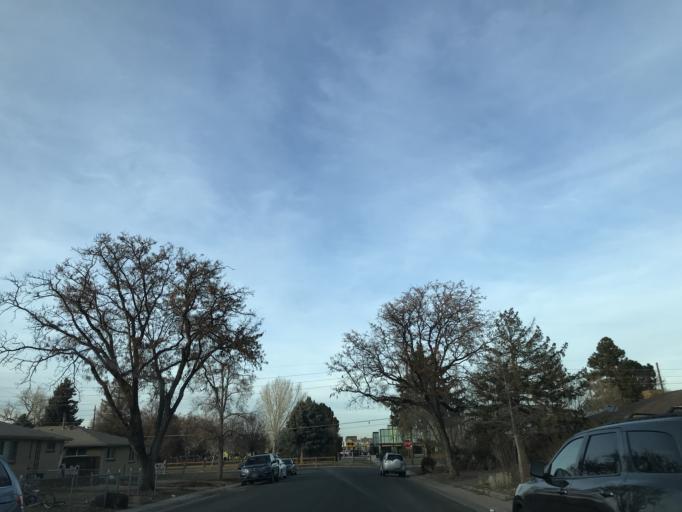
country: US
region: Colorado
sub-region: Adams County
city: Aurora
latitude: 39.7504
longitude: -104.8658
